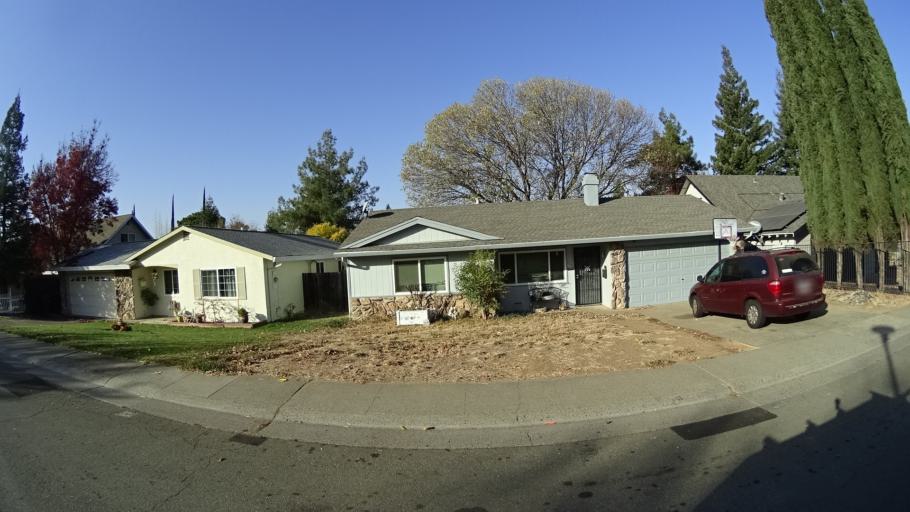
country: US
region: California
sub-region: Sacramento County
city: Citrus Heights
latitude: 38.6989
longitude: -121.2634
